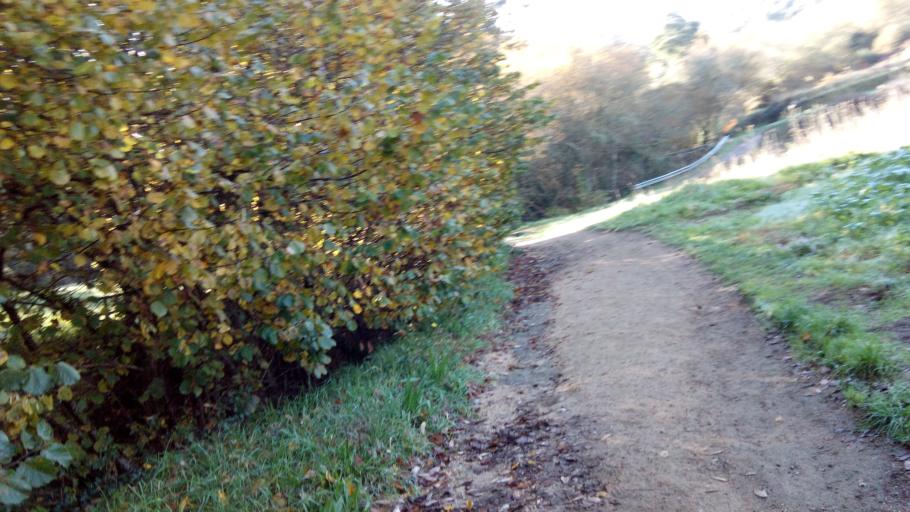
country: ES
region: Galicia
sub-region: Provincia de Pontevedra
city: Meis
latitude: 42.4766
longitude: -8.7416
